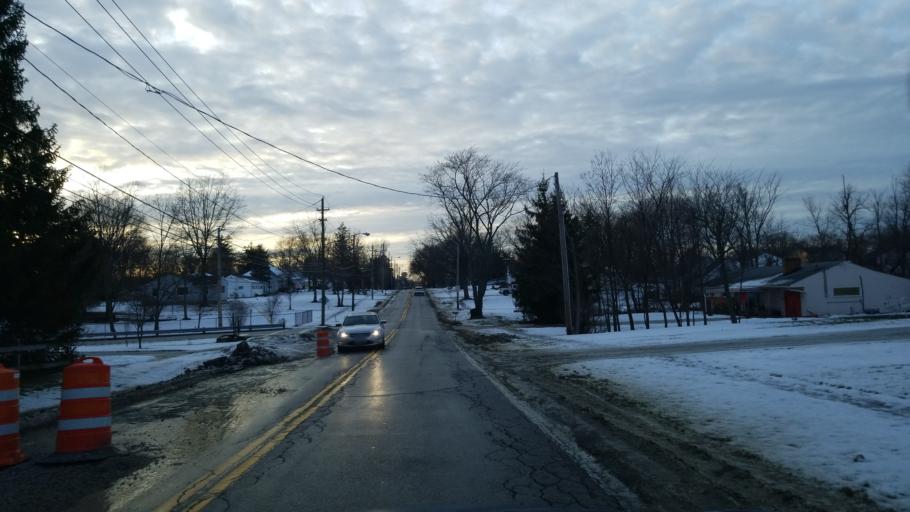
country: US
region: Ohio
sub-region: Cuyahoga County
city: Strongsville
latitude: 41.3087
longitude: -81.8279
